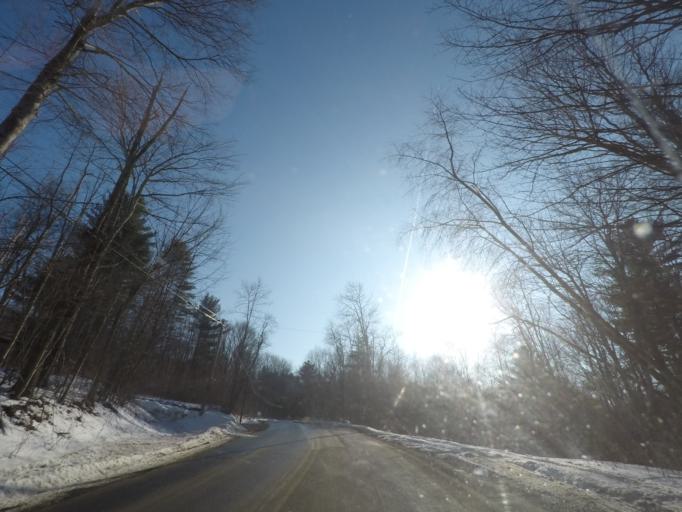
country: US
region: Massachusetts
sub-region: Berkshire County
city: Richmond
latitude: 42.5338
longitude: -73.4034
